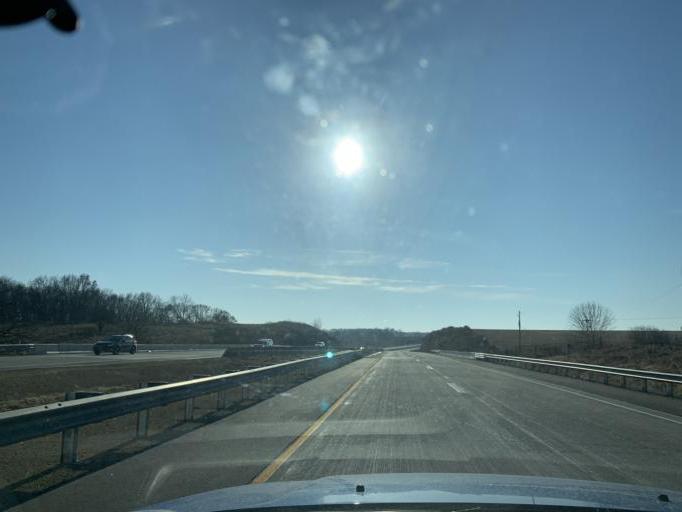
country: US
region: Wisconsin
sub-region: Iowa County
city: Dodgeville
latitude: 42.9461
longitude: -90.1176
